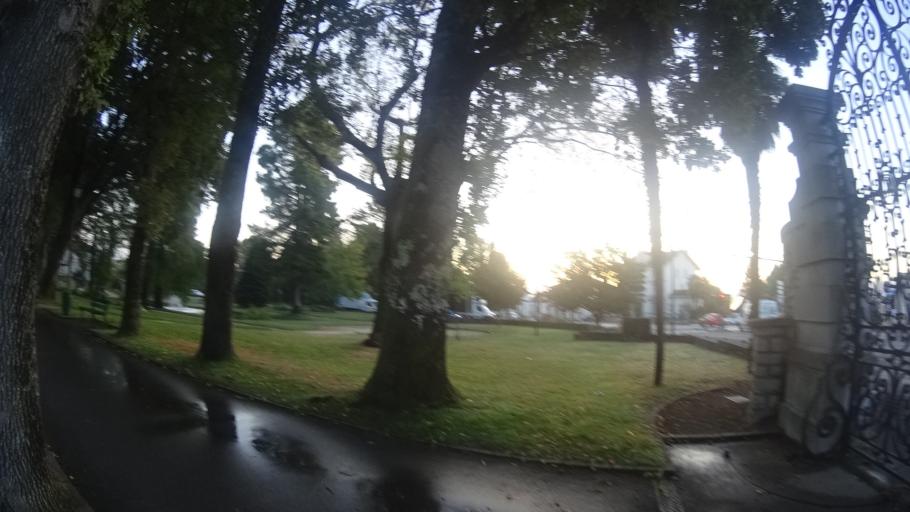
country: FR
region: Aquitaine
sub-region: Departement des Landes
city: Saint-Paul-les-Dax
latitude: 43.7240
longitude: -1.0519
